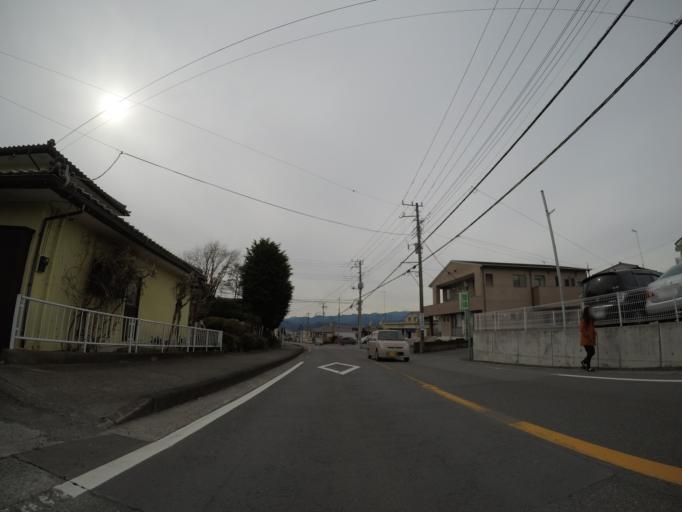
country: JP
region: Shizuoka
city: Fujinomiya
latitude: 35.2485
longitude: 138.6320
